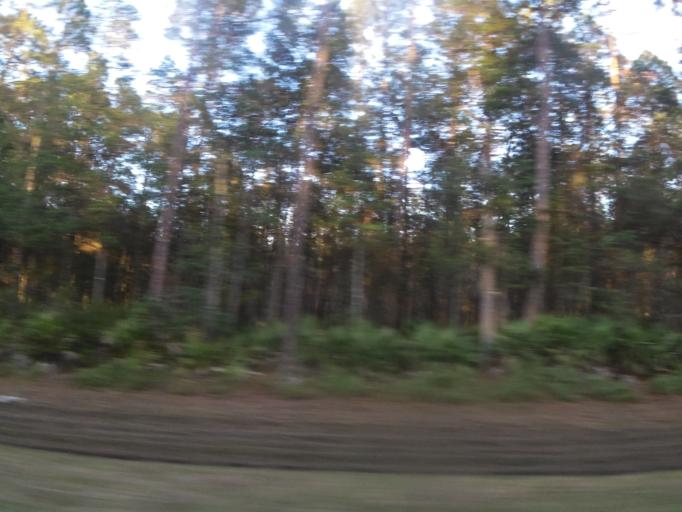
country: US
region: Florida
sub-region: Clay County
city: Green Cove Springs
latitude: 29.8812
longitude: -81.5576
